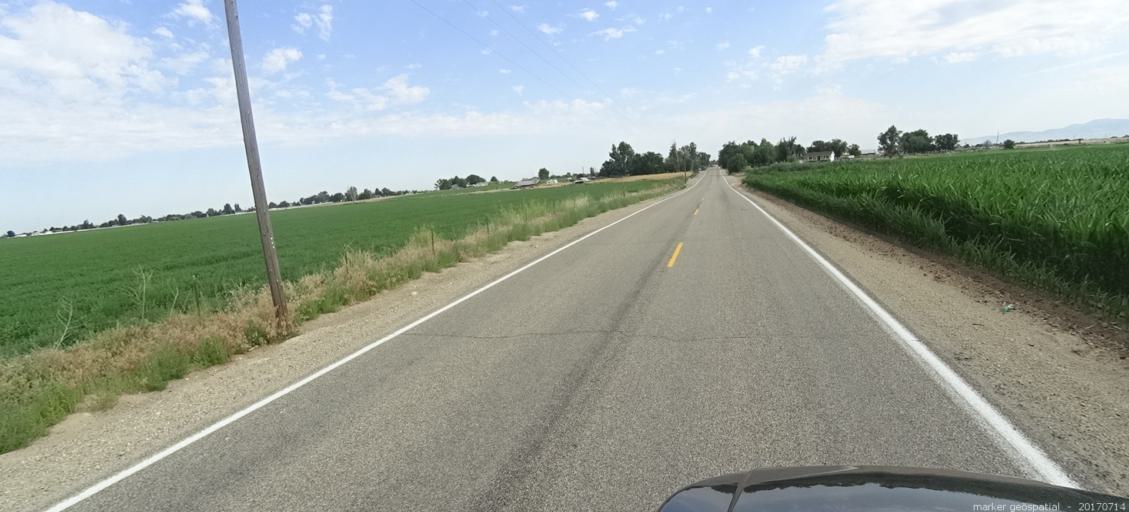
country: US
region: Idaho
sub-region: Ada County
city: Kuna
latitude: 43.4684
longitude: -116.3545
